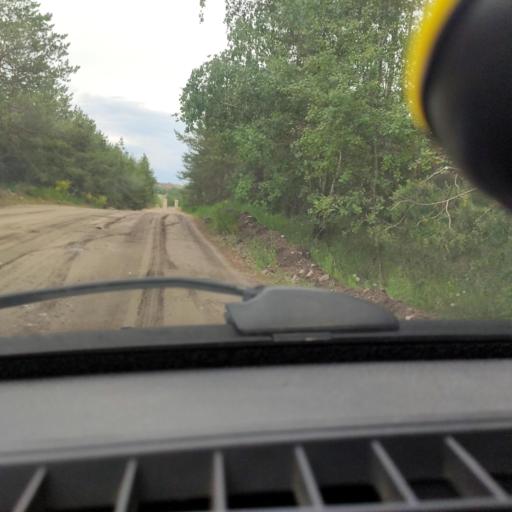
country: RU
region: Samara
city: Zhigulevsk
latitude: 53.5031
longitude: 49.5097
